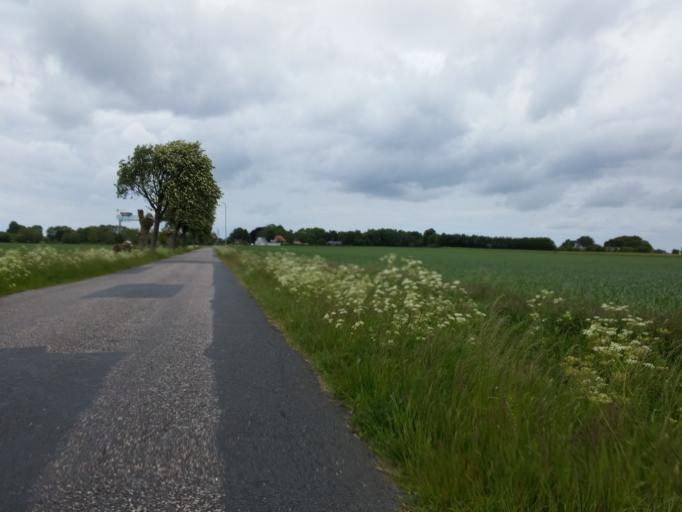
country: DK
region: South Denmark
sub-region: Kerteminde Kommune
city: Munkebo
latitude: 55.4442
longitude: 10.5203
